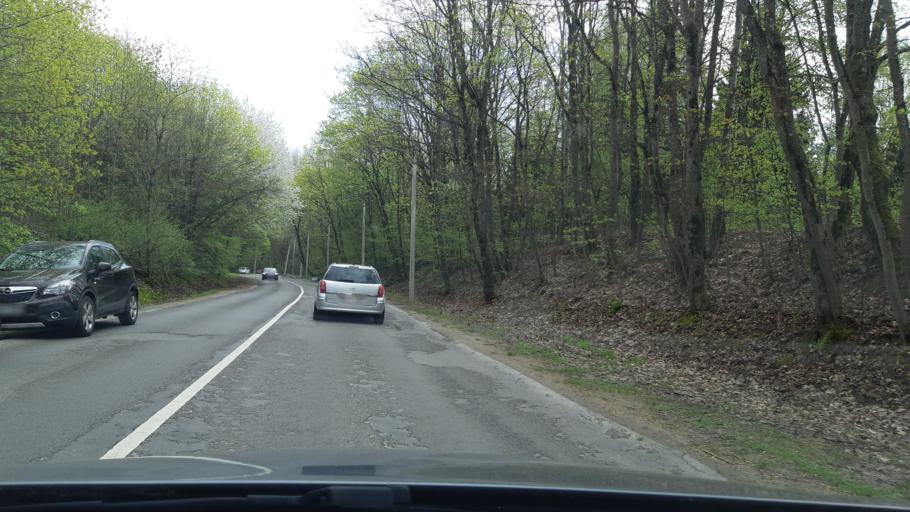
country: LT
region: Kauno apskritis
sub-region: Kaunas
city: Silainiai
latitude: 54.9241
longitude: 23.8562
